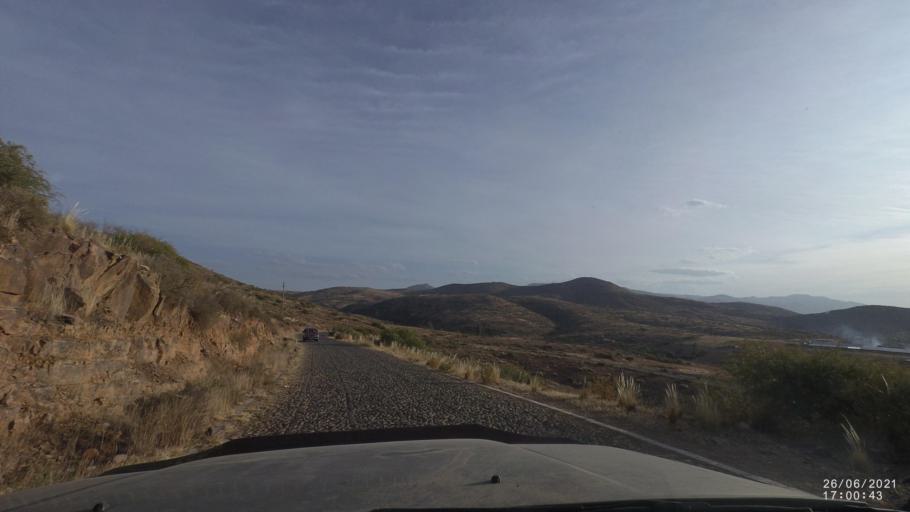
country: BO
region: Cochabamba
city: Cliza
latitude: -17.6617
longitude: -65.9089
